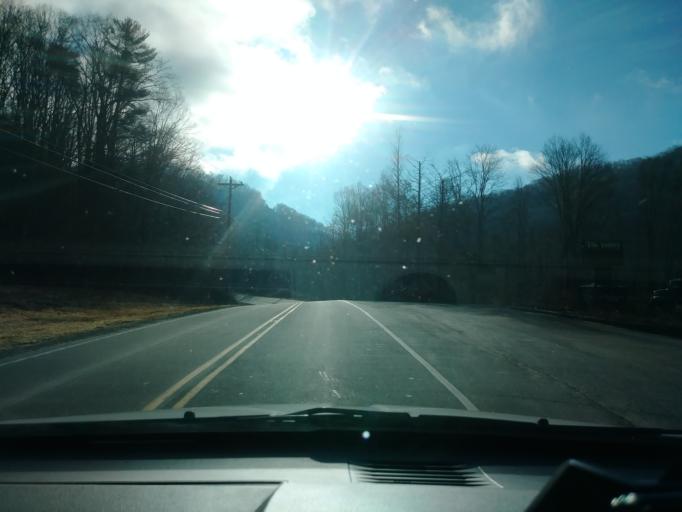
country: US
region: North Carolina
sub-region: Avery County
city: Banner Elk
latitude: 36.1732
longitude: -81.9161
